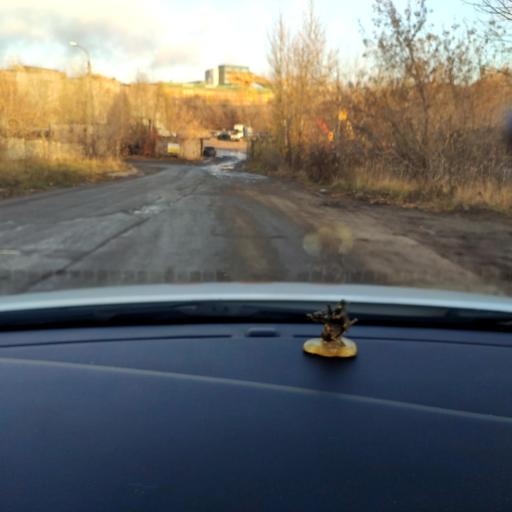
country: RU
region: Tatarstan
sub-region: Gorod Kazan'
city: Kazan
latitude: 55.7774
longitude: 49.1838
